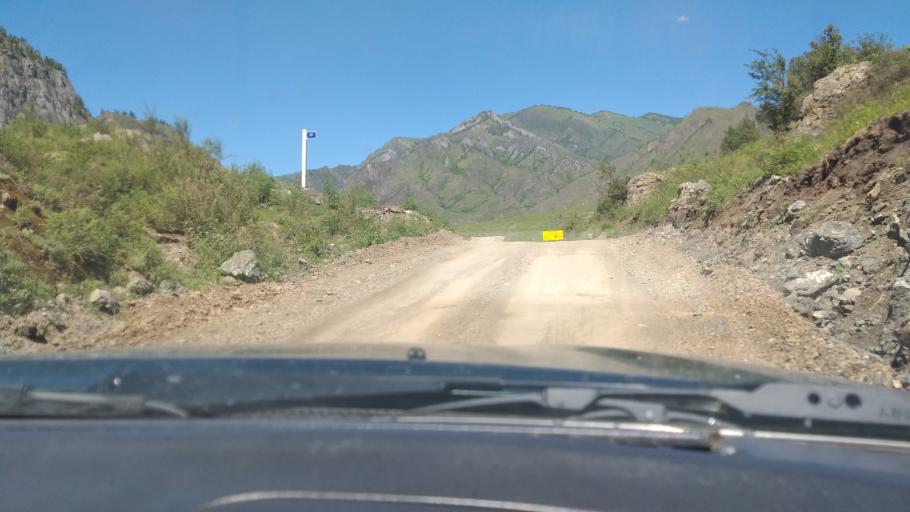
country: RU
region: Altay
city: Chemal
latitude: 51.2077
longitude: 86.0861
